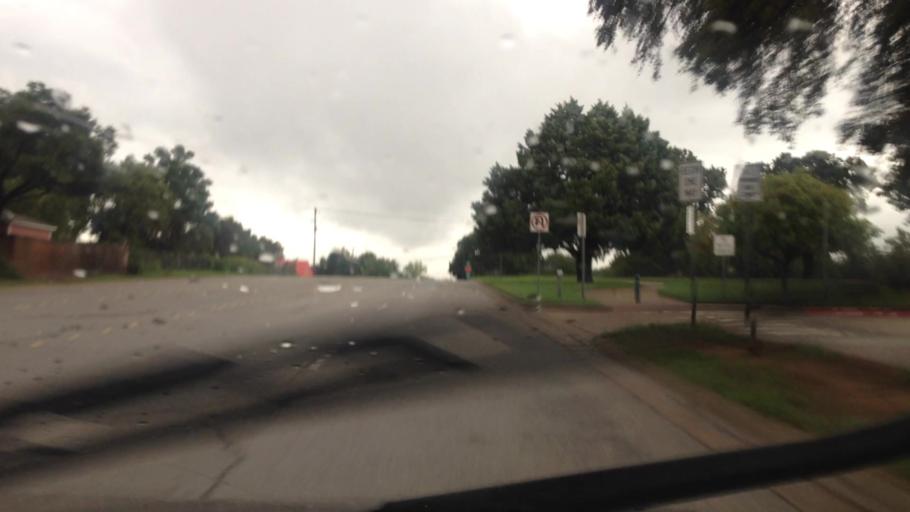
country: US
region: Texas
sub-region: Tarrant County
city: North Richland Hills
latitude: 32.8658
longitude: -97.2033
